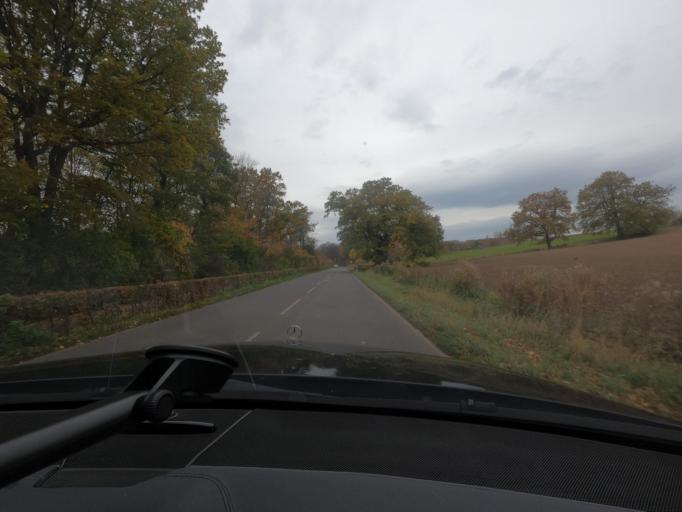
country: DE
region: North Rhine-Westphalia
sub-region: Regierungsbezirk Arnsberg
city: Mohnesee
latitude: 51.4899
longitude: 8.1668
